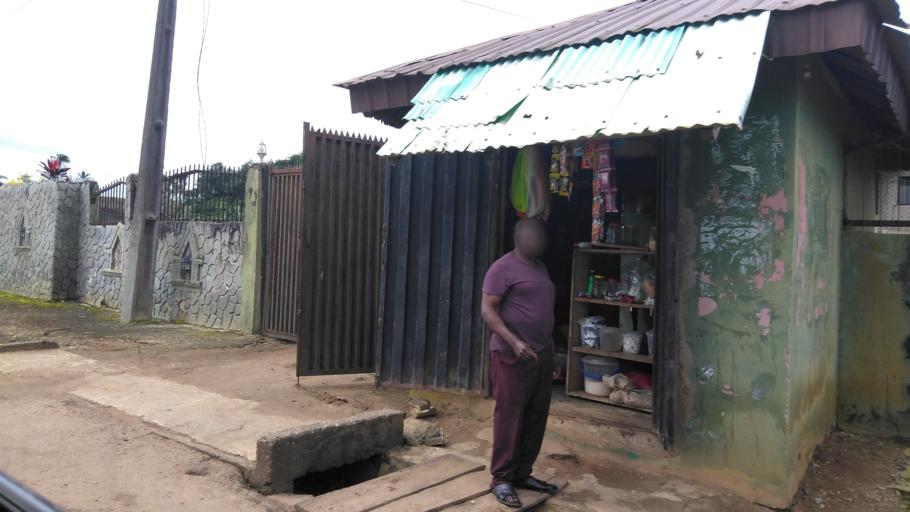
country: NG
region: Ogun
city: Abigi
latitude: 6.6042
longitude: 4.4884
